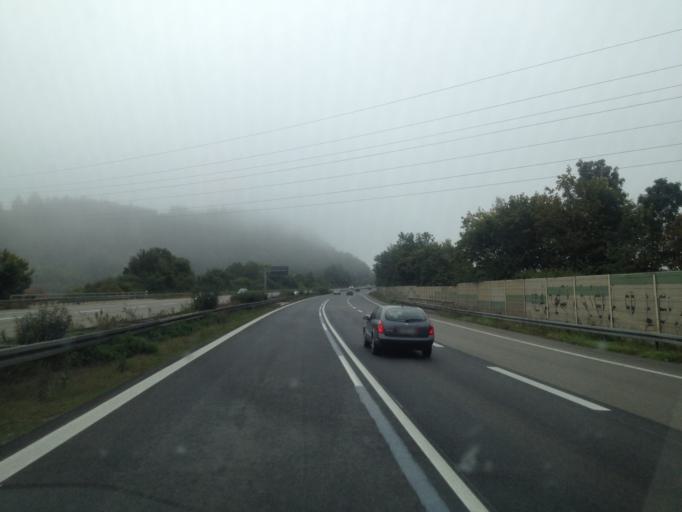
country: DE
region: Baden-Wuerttemberg
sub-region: Freiburg Region
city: Geisingen
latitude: 47.9197
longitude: 8.6753
